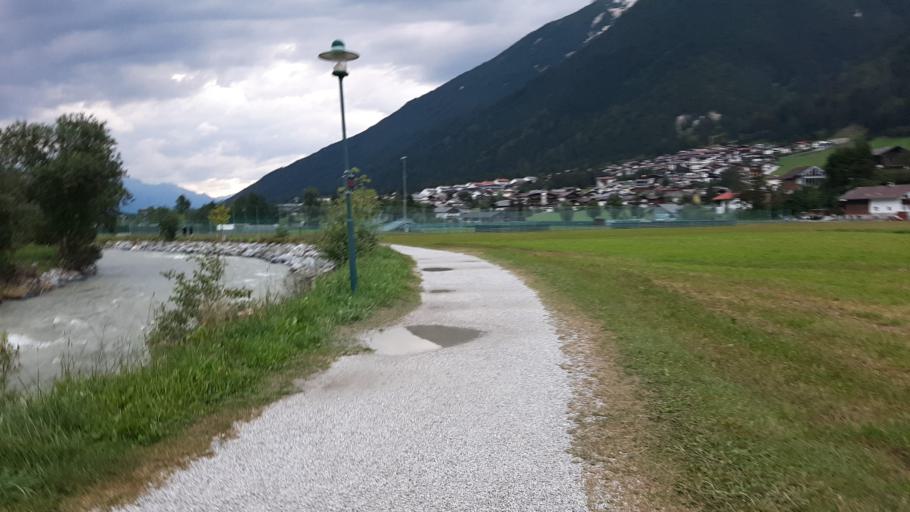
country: AT
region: Tyrol
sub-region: Politischer Bezirk Innsbruck Land
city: Neustift im Stubaital
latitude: 47.1225
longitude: 11.3276
